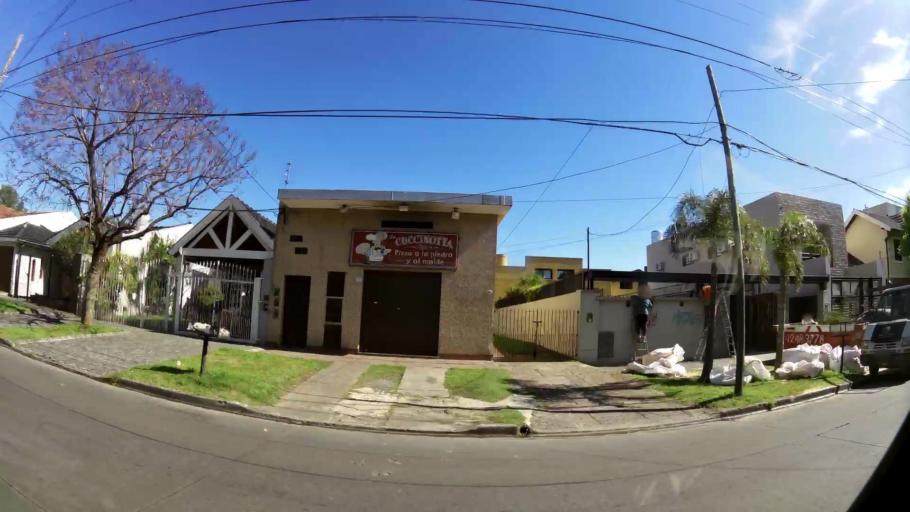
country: AR
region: Buenos Aires
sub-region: Partido de Lomas de Zamora
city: Lomas de Zamora
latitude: -34.7485
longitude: -58.4087
